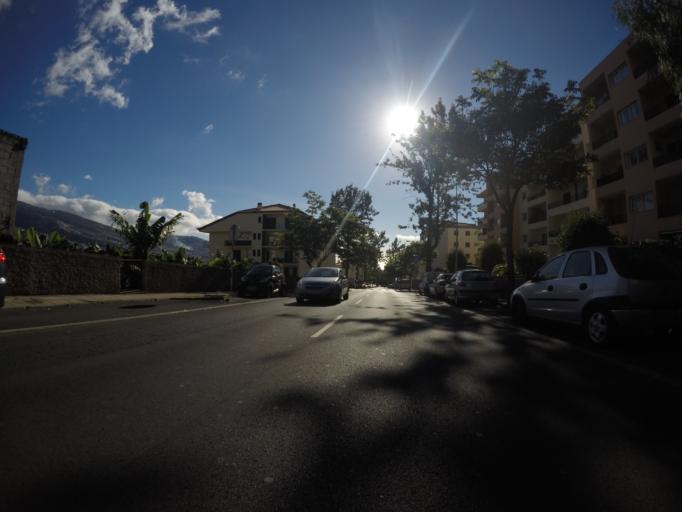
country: PT
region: Madeira
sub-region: Funchal
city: Nossa Senhora do Monte
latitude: 32.6574
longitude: -16.9261
